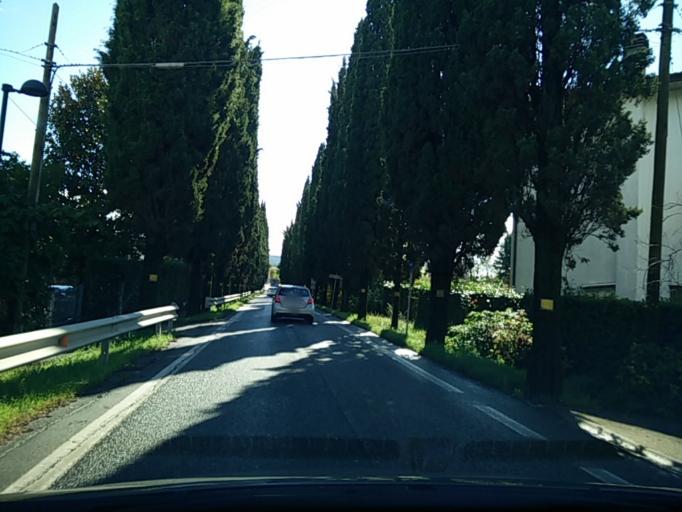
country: IT
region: Veneto
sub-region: Provincia di Treviso
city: Bigolino
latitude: 45.8630
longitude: 12.0230
